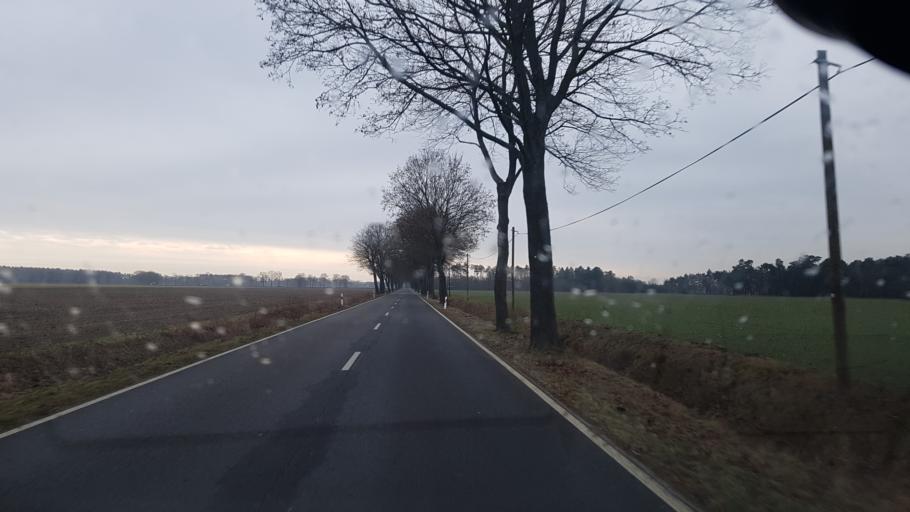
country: DE
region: Brandenburg
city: Cottbus
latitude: 51.7425
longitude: 14.4139
